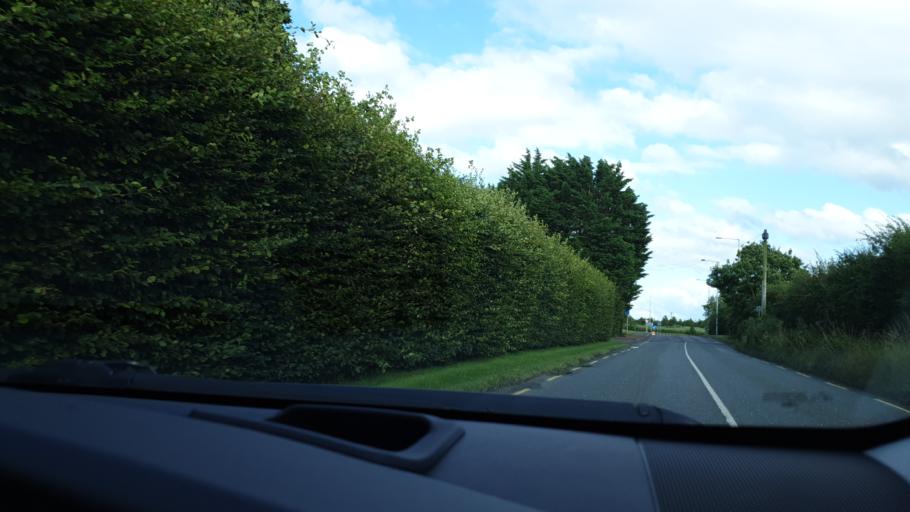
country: IE
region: Leinster
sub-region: An Mhi
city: Ashbourne
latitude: 53.4954
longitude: -6.3871
